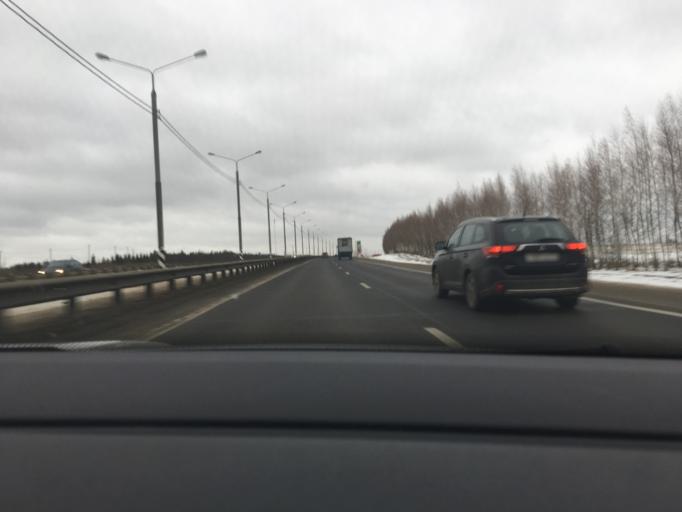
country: RU
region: Tula
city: Zaokskiy
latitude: 54.8100
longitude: 37.4822
